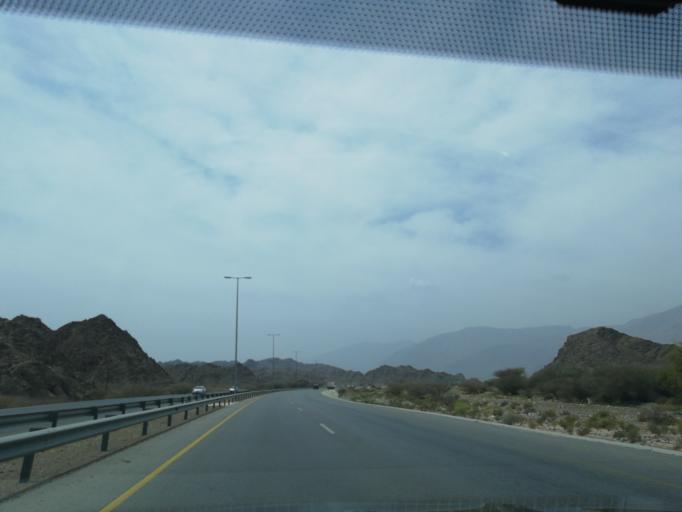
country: OM
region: Muhafazat ad Dakhiliyah
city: Sufalat Sama'il
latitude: 23.3416
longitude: 57.9983
